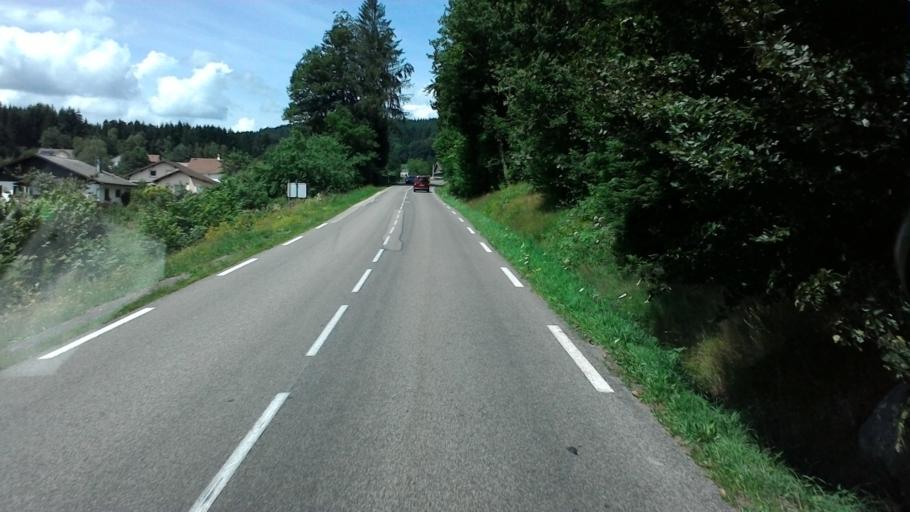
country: FR
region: Lorraine
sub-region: Departement des Vosges
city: Le Tholy
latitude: 48.0886
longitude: 6.7324
